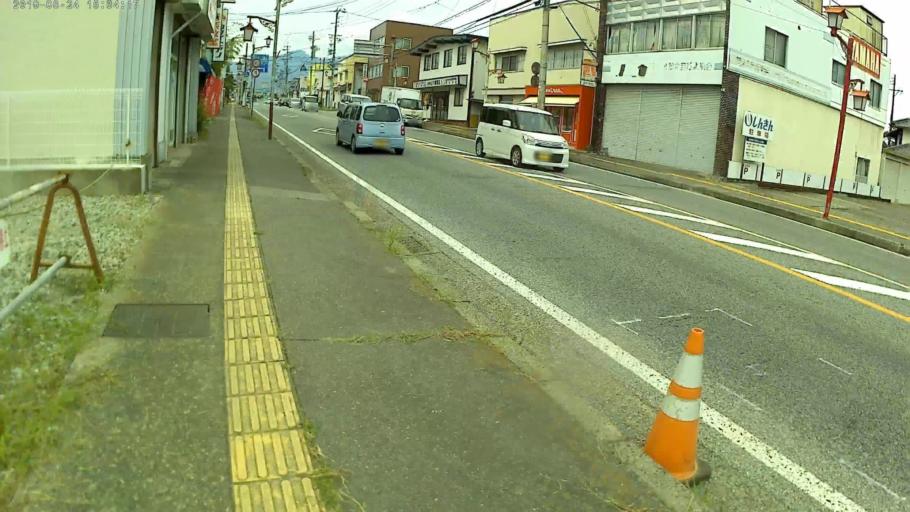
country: JP
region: Nagano
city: Saku
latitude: 36.2749
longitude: 138.4782
